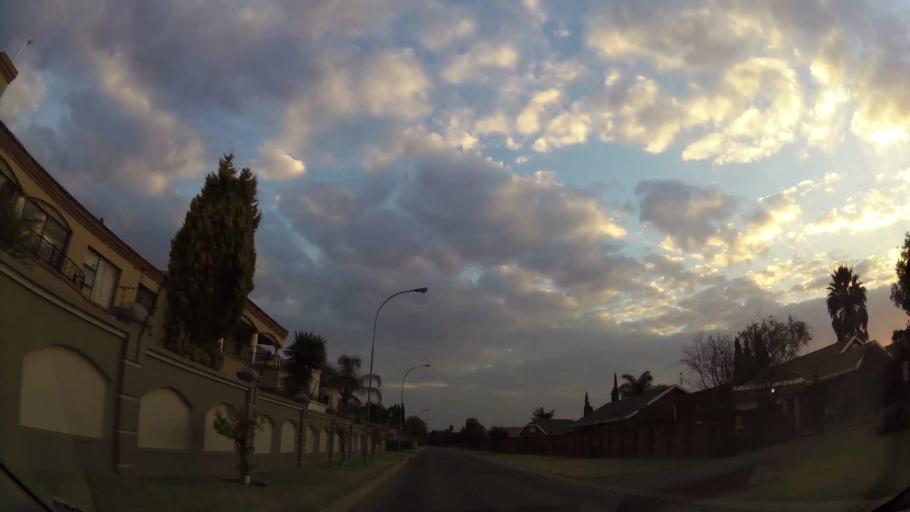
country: ZA
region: Gauteng
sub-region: Ekurhuleni Metropolitan Municipality
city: Benoni
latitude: -26.1702
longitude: 28.3098
